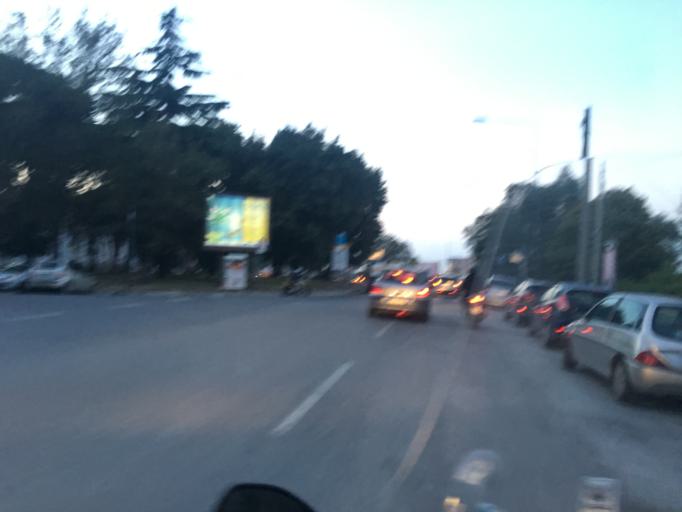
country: IT
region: Campania
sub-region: Provincia di Napoli
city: Napoli
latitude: 40.8647
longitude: 14.2271
